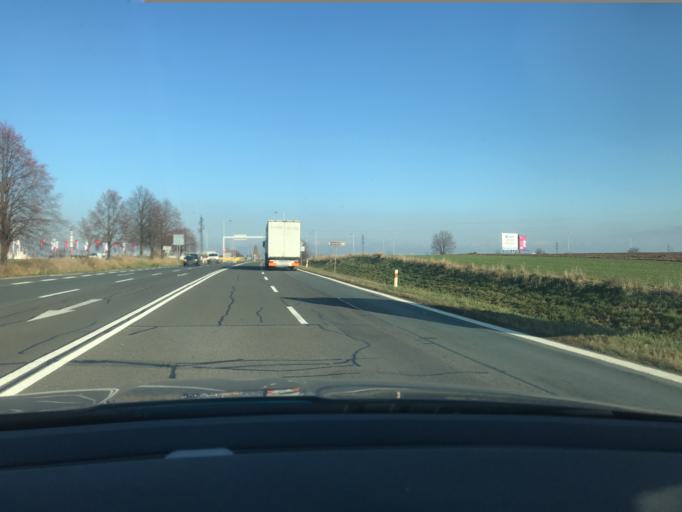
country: CZ
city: Predmerice nad Labem
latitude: 50.2289
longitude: 15.7903
